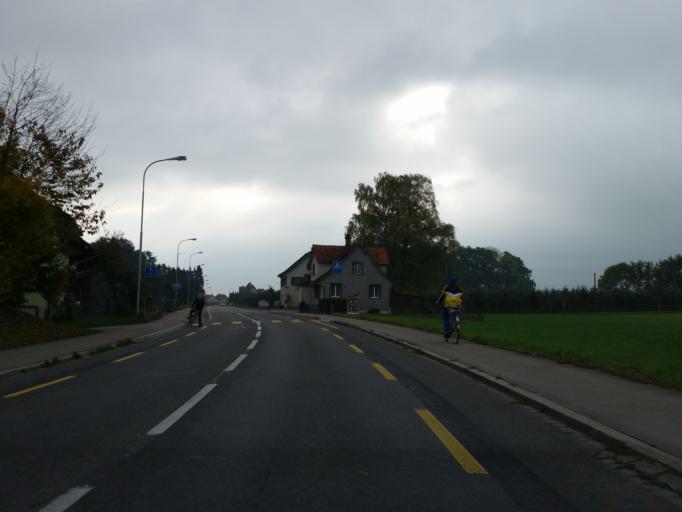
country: CH
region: Thurgau
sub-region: Arbon District
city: Egnach
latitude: 47.5403
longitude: 9.3800
